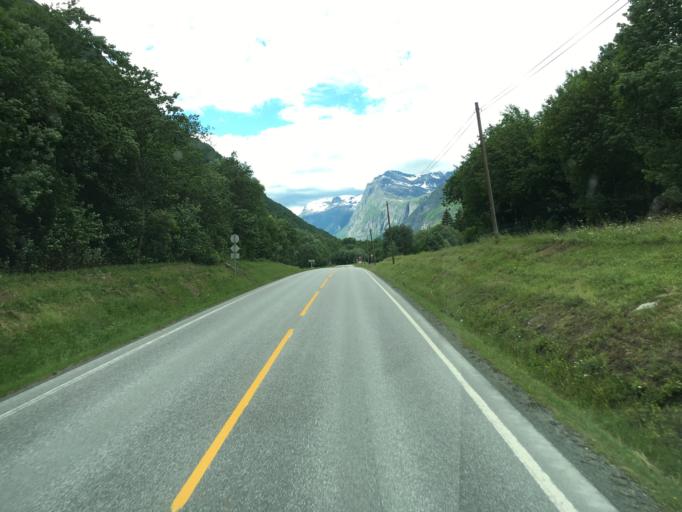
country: NO
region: More og Romsdal
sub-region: Sunndal
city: Sunndalsora
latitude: 62.6073
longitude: 8.9299
